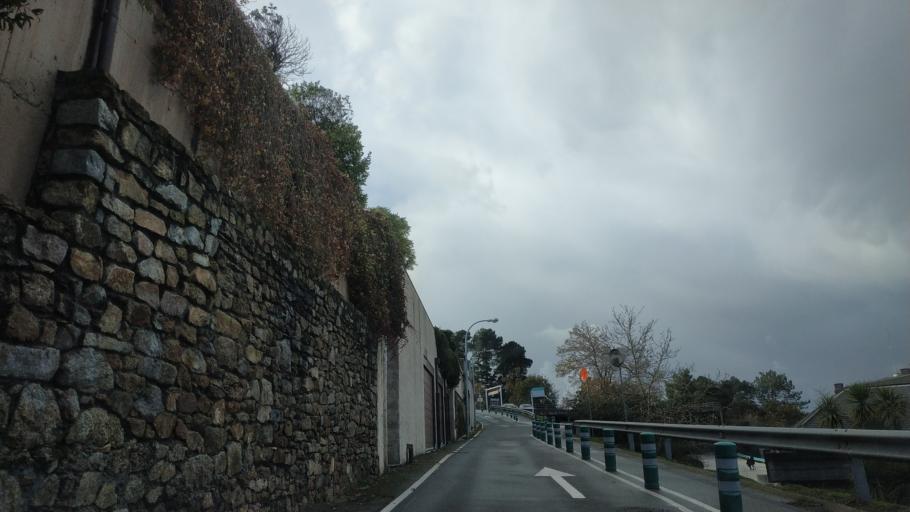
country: ES
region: Galicia
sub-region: Provincia da Coruna
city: Culleredo
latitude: 43.3282
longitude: -8.3996
